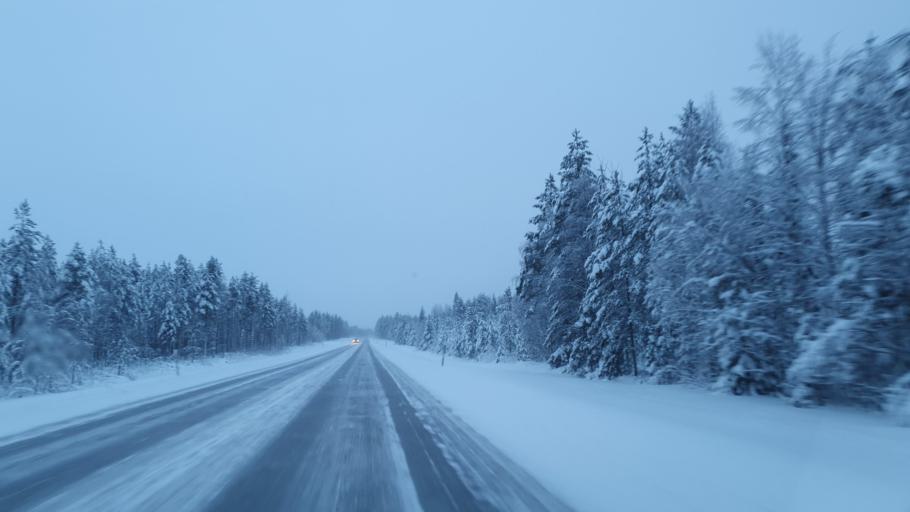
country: FI
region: Kainuu
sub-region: Kajaani
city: Vaala
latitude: 64.5523
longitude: 27.0559
